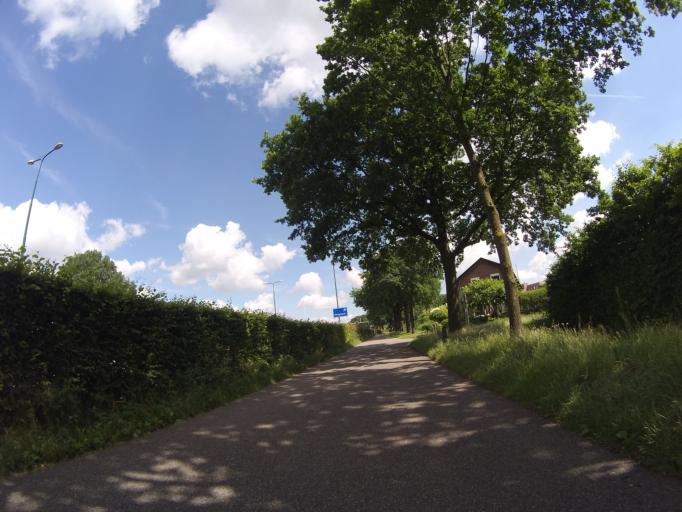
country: NL
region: Utrecht
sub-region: Gemeente Amersfoort
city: Hoogland
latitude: 52.1801
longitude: 5.3699
